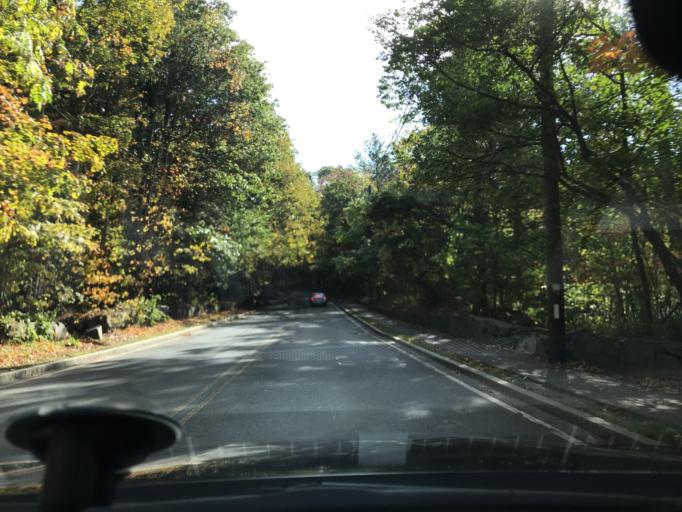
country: US
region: Massachusetts
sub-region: Suffolk County
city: Jamaica Plain
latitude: 42.3016
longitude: -71.1386
